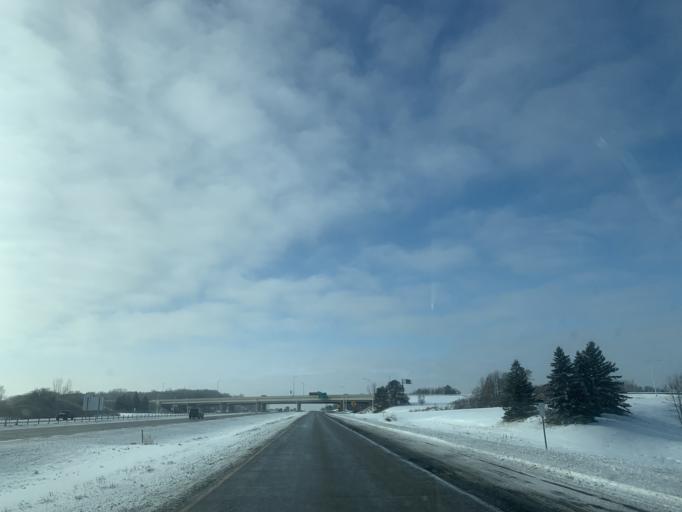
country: US
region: Minnesota
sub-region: Dakota County
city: Apple Valley
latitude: 44.7809
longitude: -93.2139
